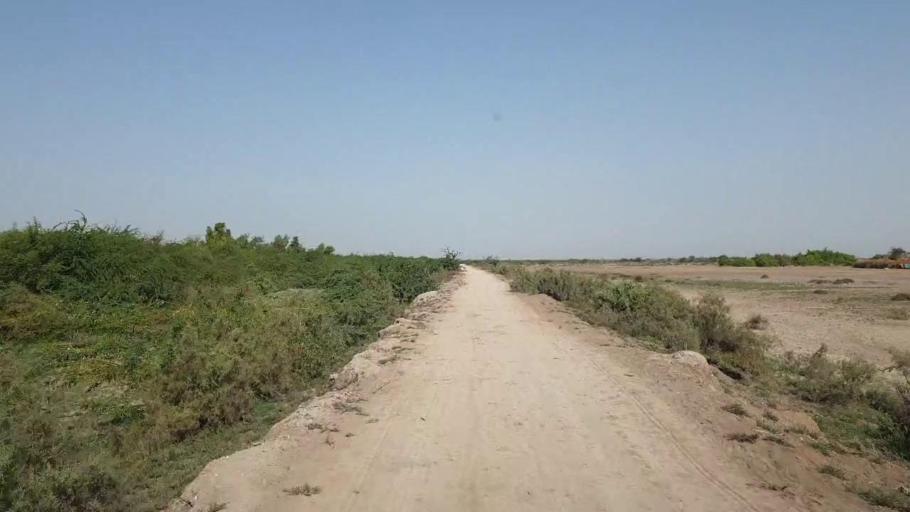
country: PK
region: Sindh
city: Tando Bago
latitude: 24.6492
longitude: 69.0713
